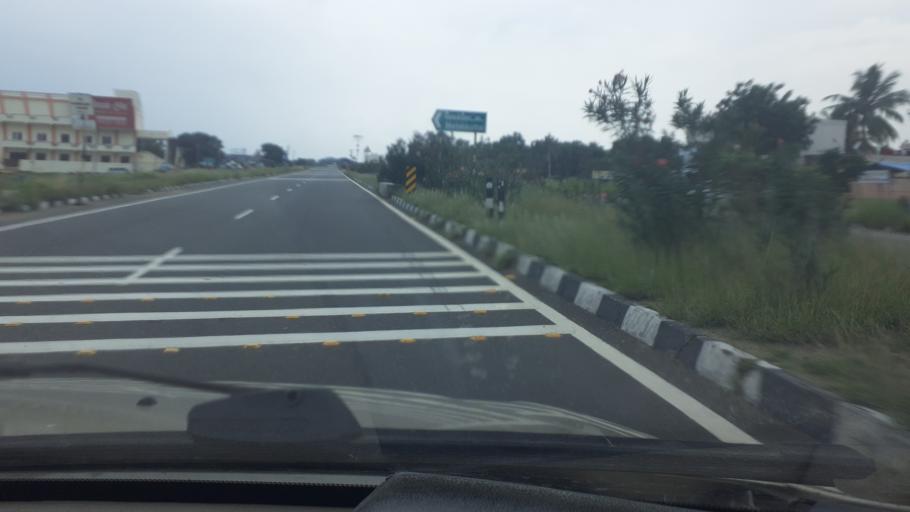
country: IN
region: Tamil Nadu
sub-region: Madurai
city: Tirupparangunram
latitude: 9.7942
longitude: 77.9843
